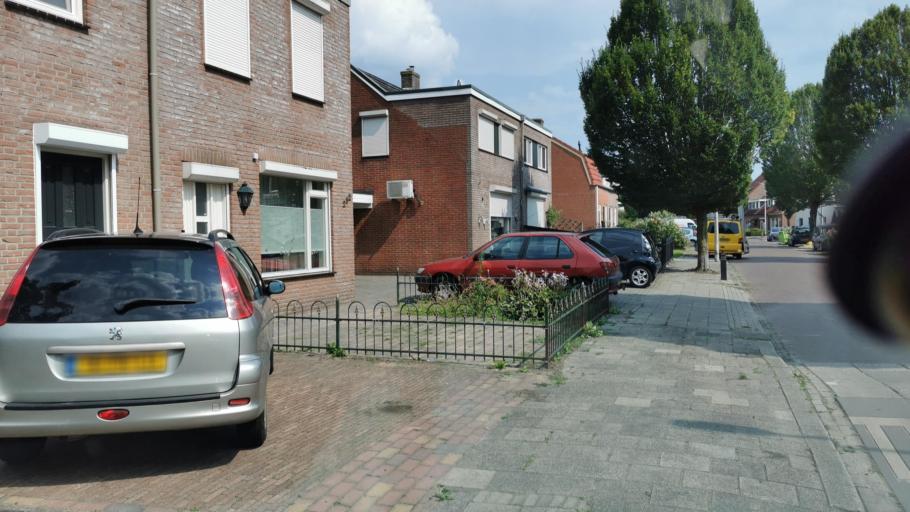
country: NL
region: Overijssel
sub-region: Gemeente Losser
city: Losser
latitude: 52.2212
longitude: 6.9606
